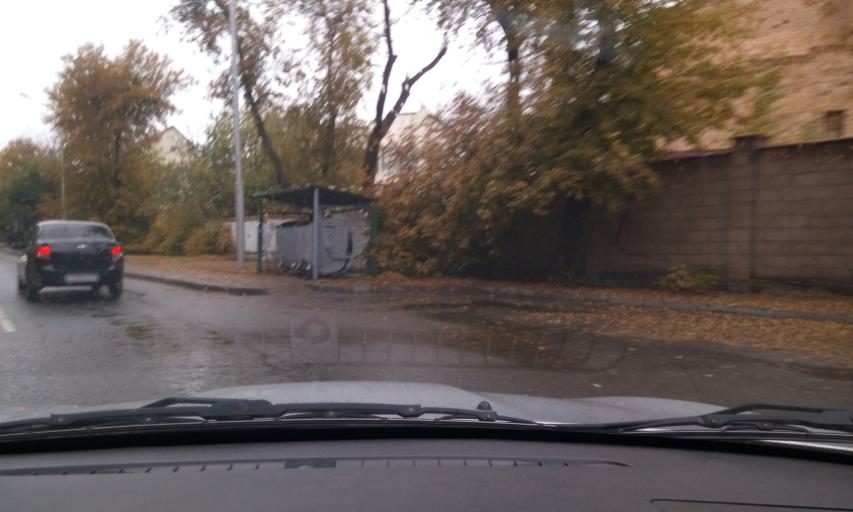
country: KZ
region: Astana Qalasy
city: Astana
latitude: 51.1445
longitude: 71.4307
